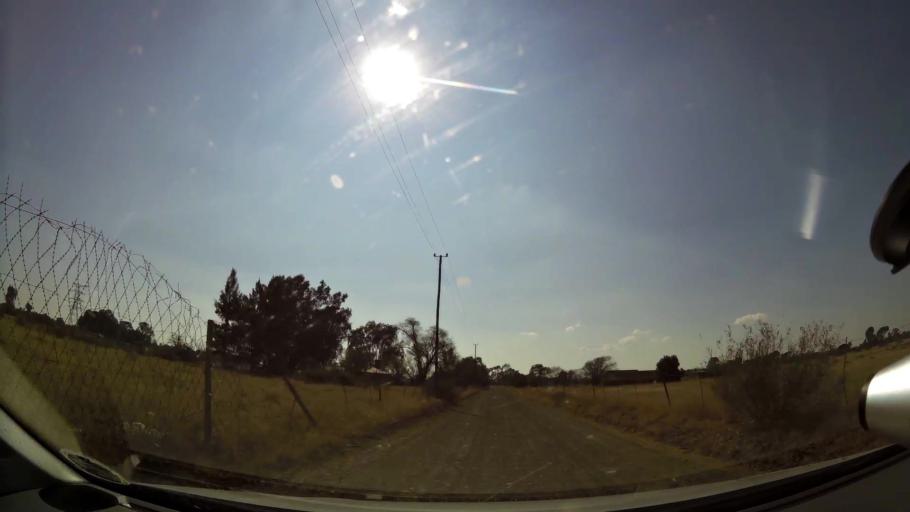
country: ZA
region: Orange Free State
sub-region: Mangaung Metropolitan Municipality
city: Bloemfontein
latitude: -29.1619
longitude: 26.3116
